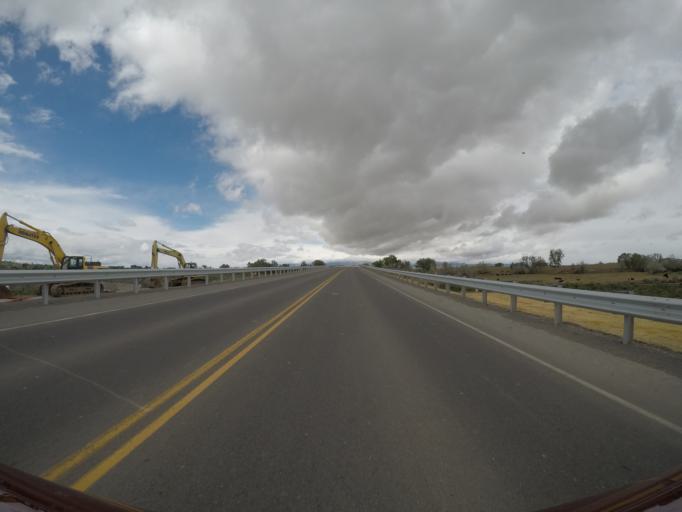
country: US
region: Wyoming
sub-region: Big Horn County
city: Lovell
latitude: 44.8480
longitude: -108.4446
